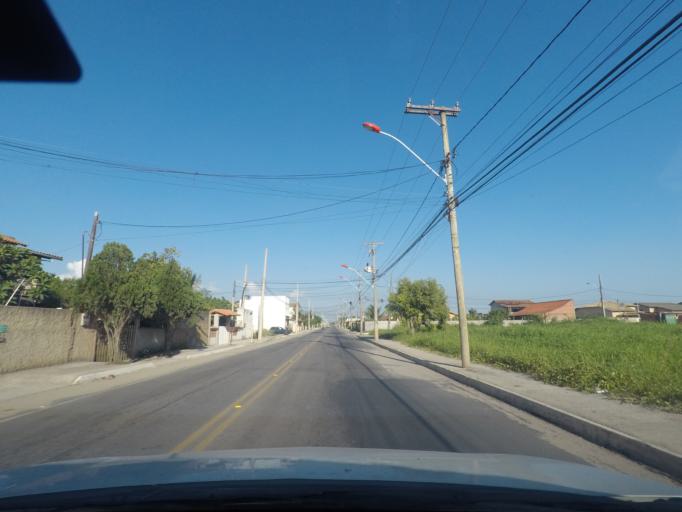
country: BR
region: Rio de Janeiro
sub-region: Marica
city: Marica
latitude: -22.9567
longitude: -42.9493
